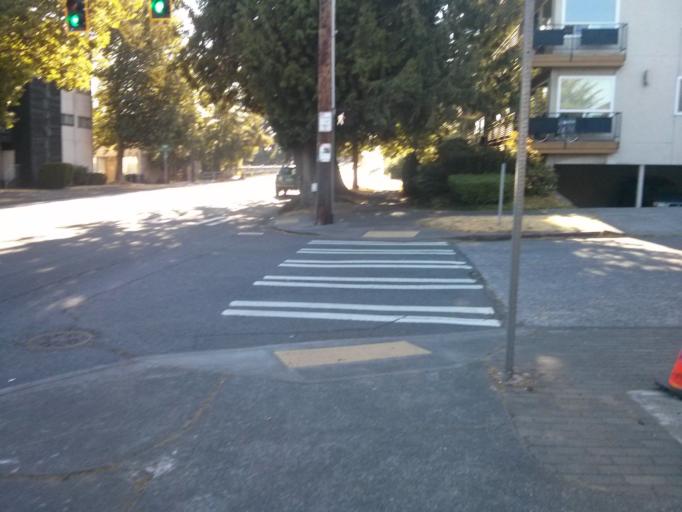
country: US
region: Washington
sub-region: King County
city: Seattle
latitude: 47.5811
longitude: -122.3840
